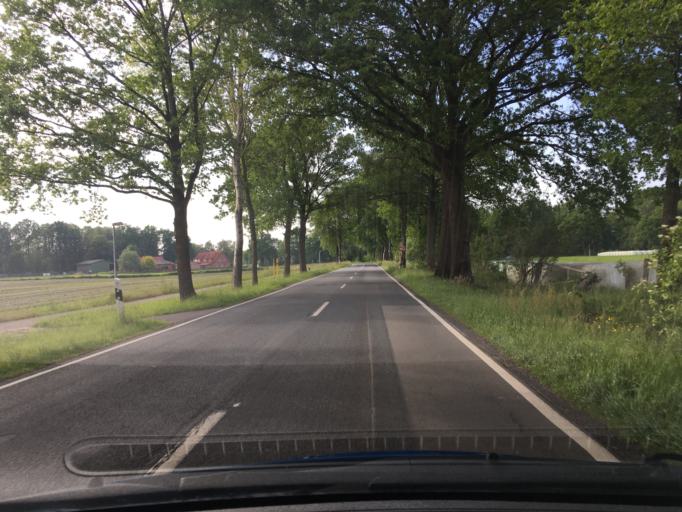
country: DE
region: Lower Saxony
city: Kalbe
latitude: 53.2843
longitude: 9.5603
